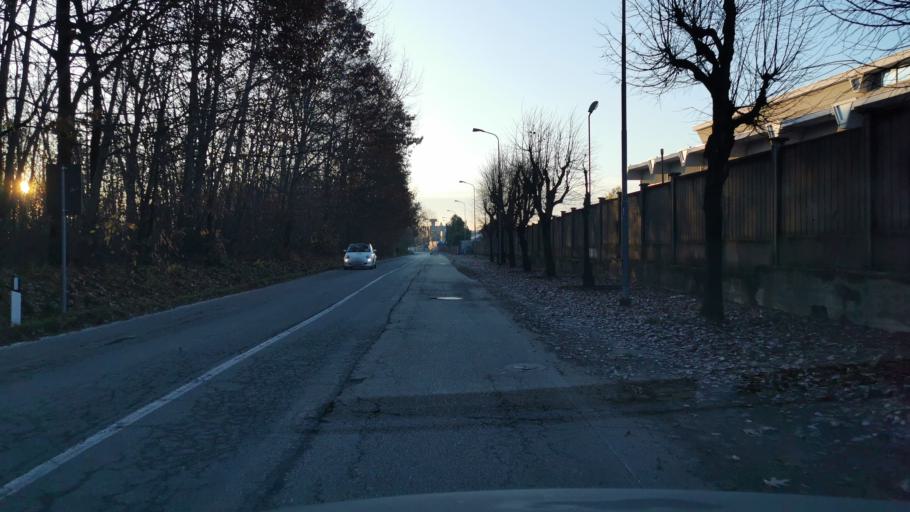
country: IT
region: Piedmont
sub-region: Provincia di Torino
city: La Cassa
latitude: 45.1715
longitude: 7.5209
